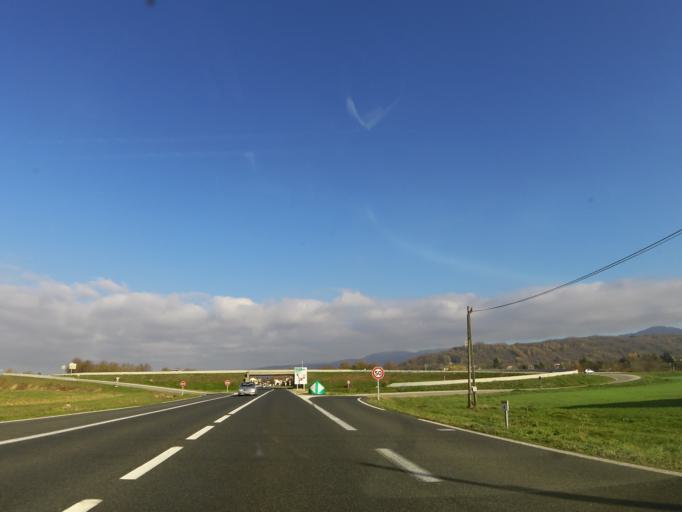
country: FR
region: Rhone-Alpes
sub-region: Departement de l'Ain
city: Saint-Denis-en-Bugey
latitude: 45.9463
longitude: 5.3166
